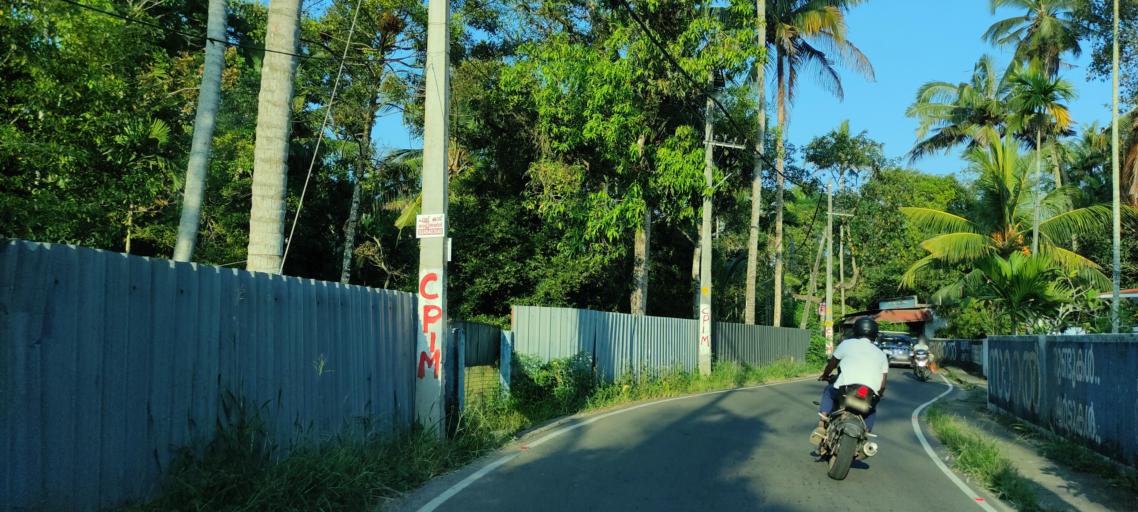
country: IN
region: Kerala
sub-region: Alappuzha
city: Shertallai
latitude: 9.6935
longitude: 76.3449
